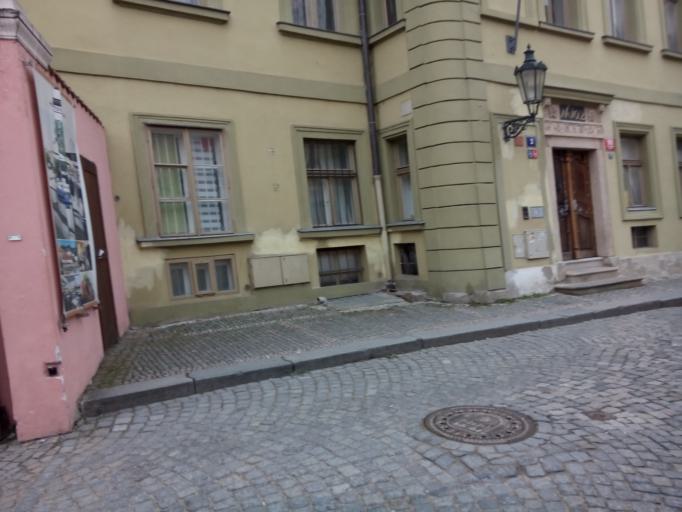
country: CZ
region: Praha
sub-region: Praha 1
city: Mala Strana
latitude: 50.0881
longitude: 14.4100
